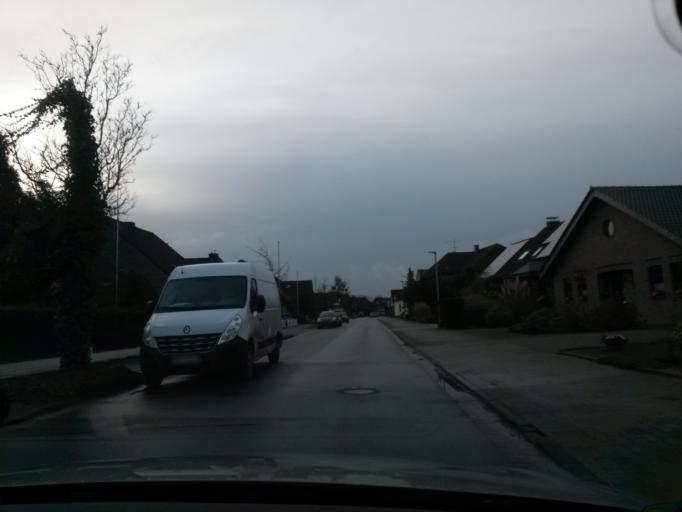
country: DE
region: North Rhine-Westphalia
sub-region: Regierungsbezirk Dusseldorf
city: Alpen
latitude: 51.6221
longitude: 6.5321
